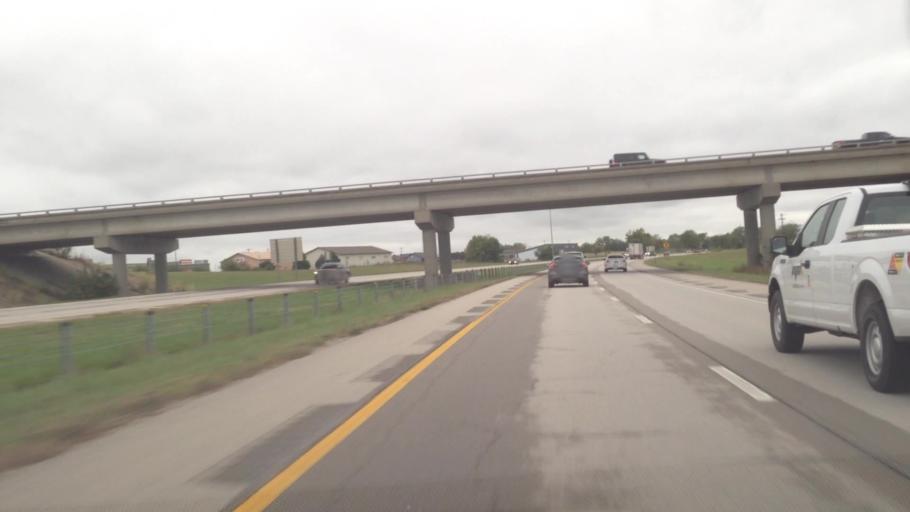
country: US
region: Kansas
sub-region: Douglas County
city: Eudora
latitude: 38.9305
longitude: -95.0888
